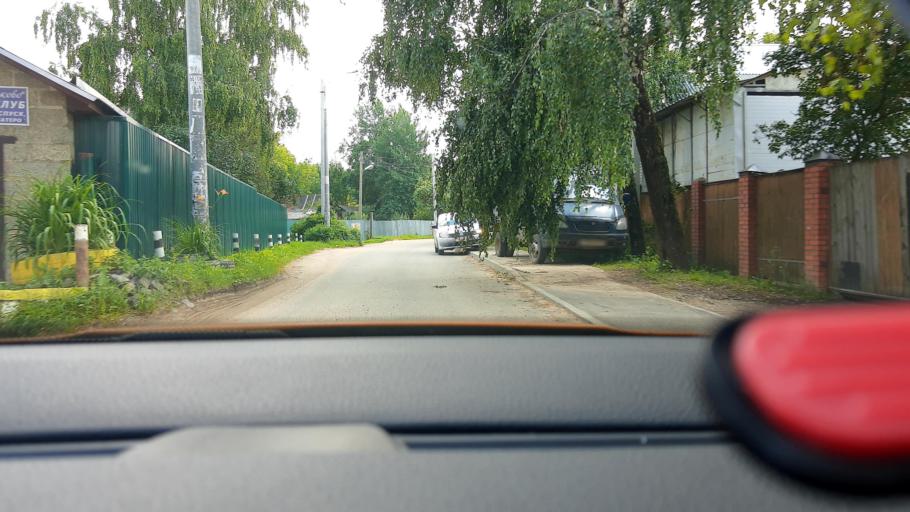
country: RU
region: Moskovskaya
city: Povedniki
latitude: 55.9990
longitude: 37.5916
